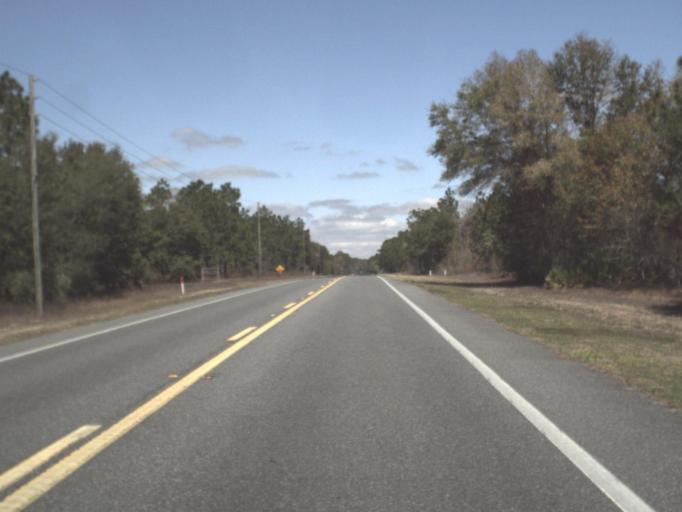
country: US
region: Florida
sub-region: Wakulla County
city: Crawfordville
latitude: 30.0654
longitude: -84.3887
